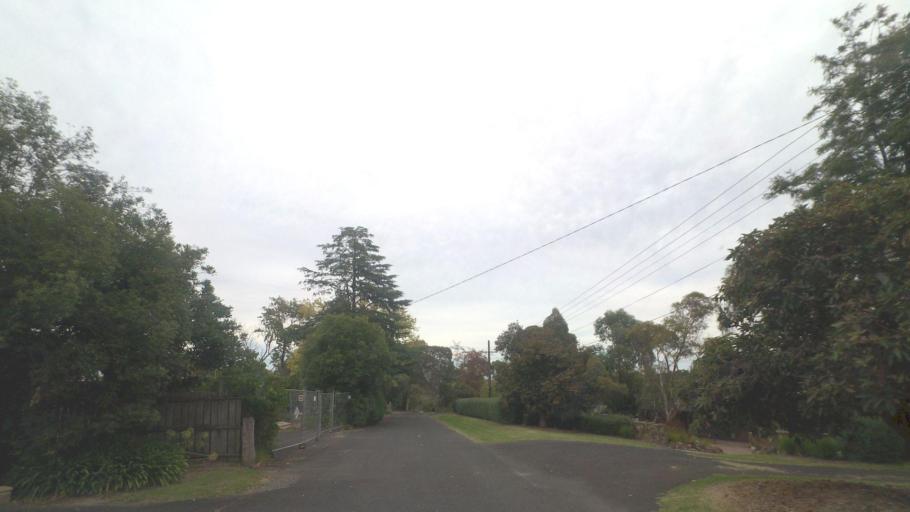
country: AU
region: Victoria
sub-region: Nillumbik
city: Eltham
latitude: -37.7498
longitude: 145.1829
